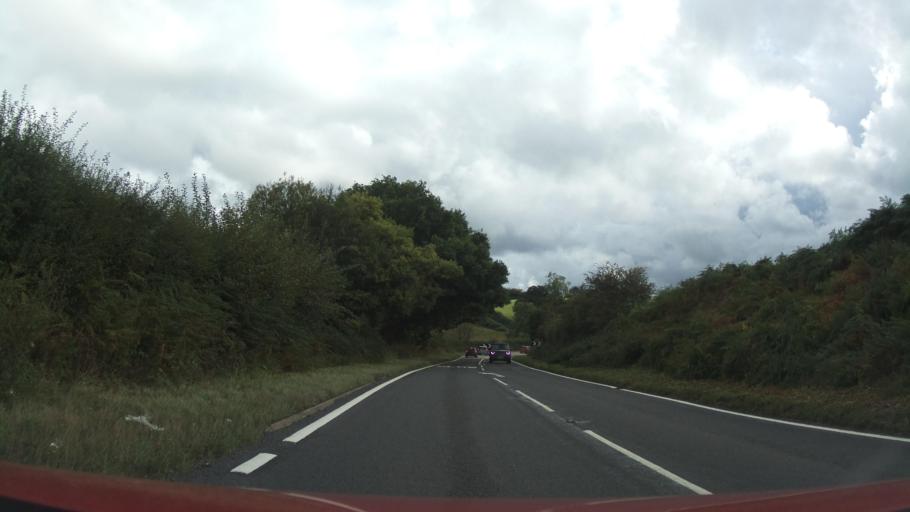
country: GB
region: England
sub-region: Shropshire
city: Bridgnorth
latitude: 52.5669
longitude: -2.3917
